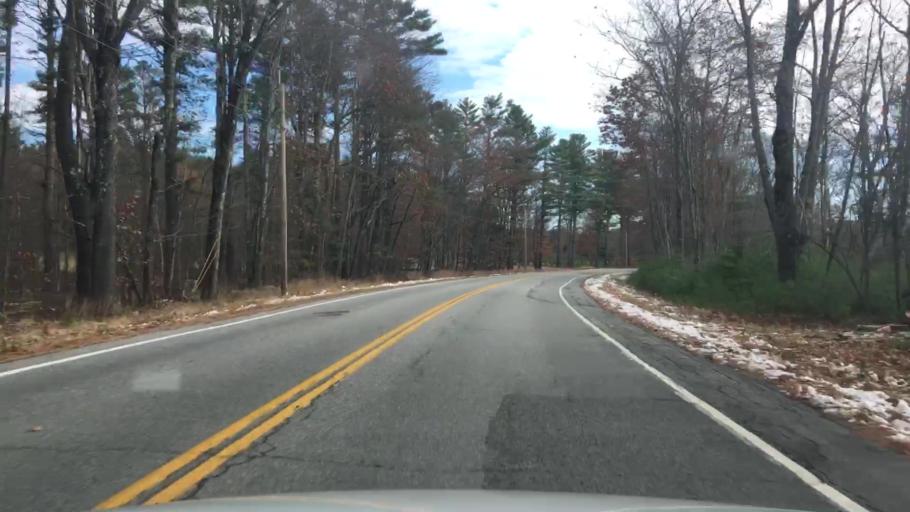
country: US
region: Maine
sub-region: Kennebec County
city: Wayne
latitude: 44.3516
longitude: -70.1069
